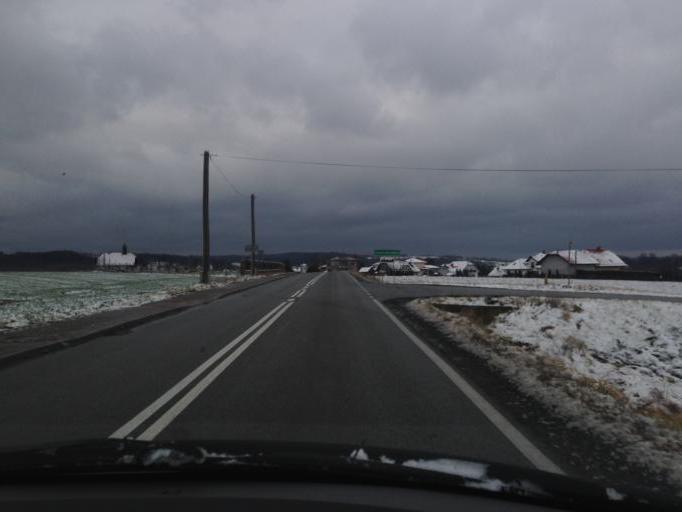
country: PL
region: Lesser Poland Voivodeship
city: Stary Wisnicz
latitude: 49.8549
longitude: 20.5192
